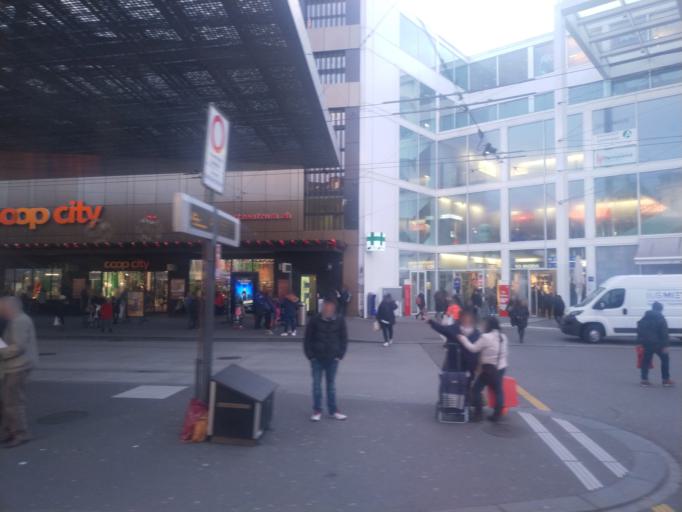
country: CH
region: Zurich
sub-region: Bezirk Winterthur
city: Winterthur
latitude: 47.4993
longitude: 8.7235
